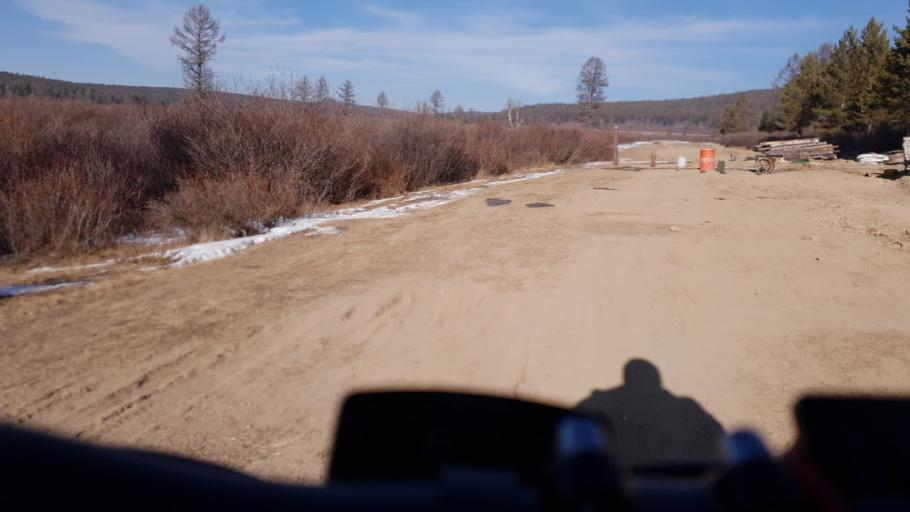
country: MN
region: Ulaanbaatar
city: Ulaanbaatar
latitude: 48.1580
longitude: 106.8816
